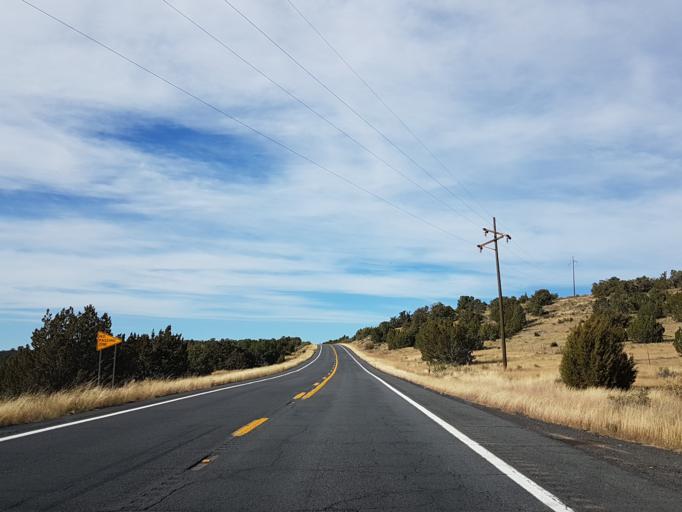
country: US
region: Arizona
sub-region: Coconino County
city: Williams
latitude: 35.4673
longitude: -112.1734
